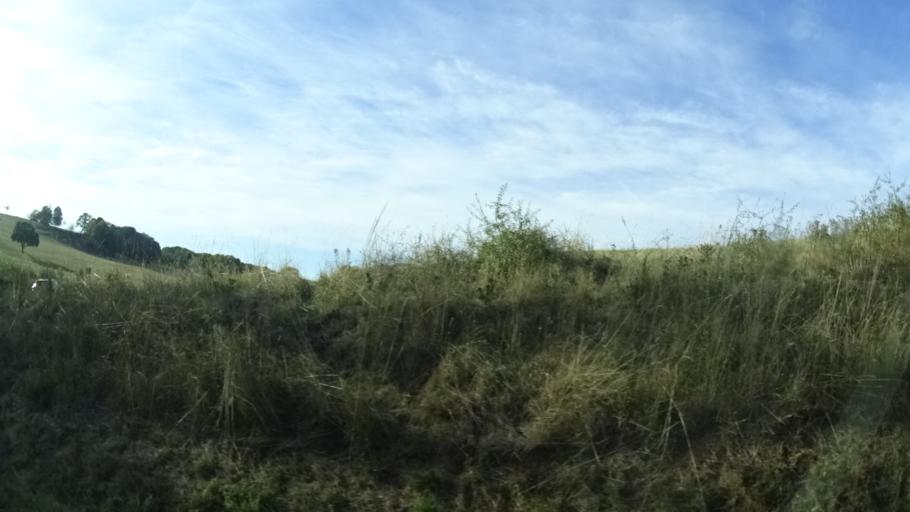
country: DE
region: Hesse
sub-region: Regierungsbezirk Giessen
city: Freiensteinau
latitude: 50.4023
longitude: 9.4548
